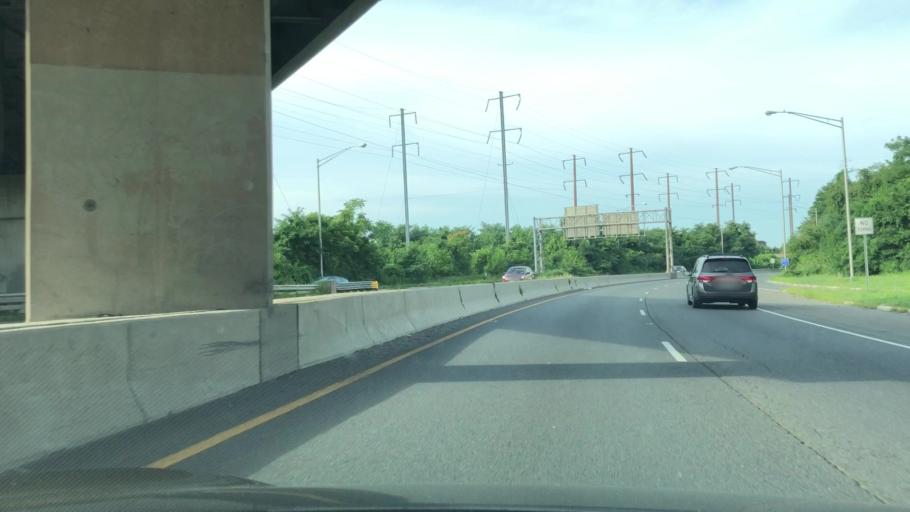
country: US
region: New Jersey
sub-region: Mercer County
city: Trenton
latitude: 40.2162
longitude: -74.7577
